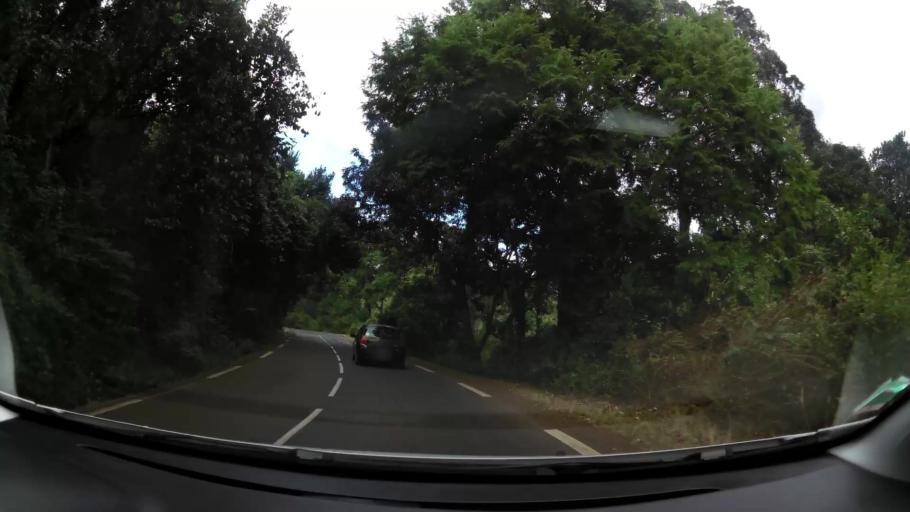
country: YT
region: Dembeni
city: Dembeni
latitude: -12.8401
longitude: 45.1669
